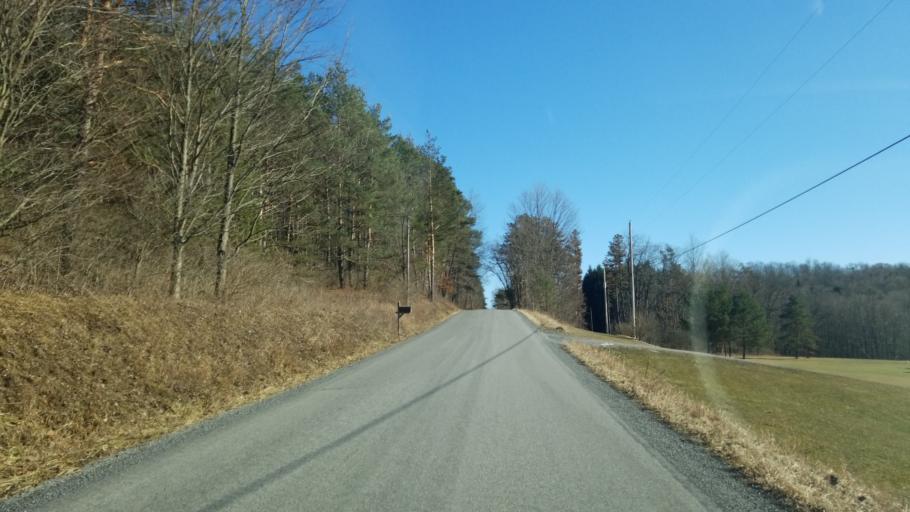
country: US
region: Pennsylvania
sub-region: Jefferson County
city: Sykesville
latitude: 41.0496
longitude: -78.7905
